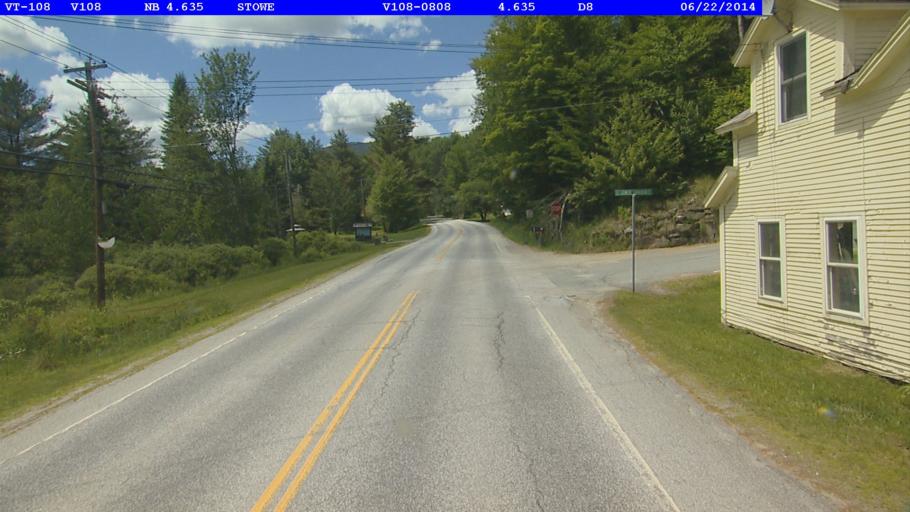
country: US
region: Vermont
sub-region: Lamoille County
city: Morristown
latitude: 44.5003
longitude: -72.7475
